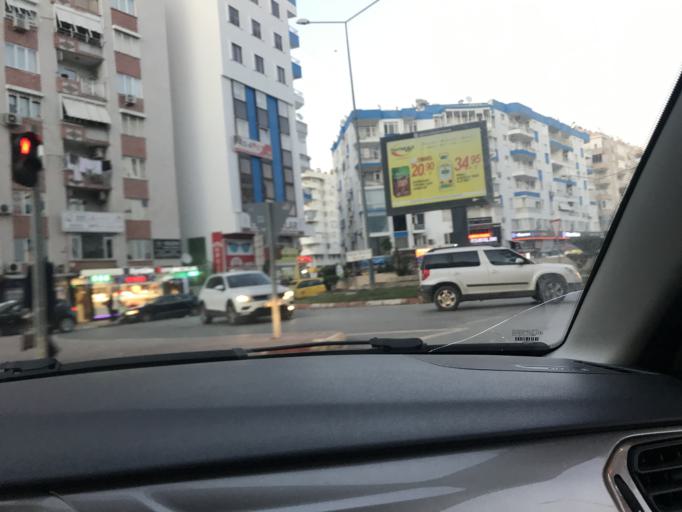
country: TR
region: Antalya
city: Antalya
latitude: 36.8909
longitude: 30.6949
